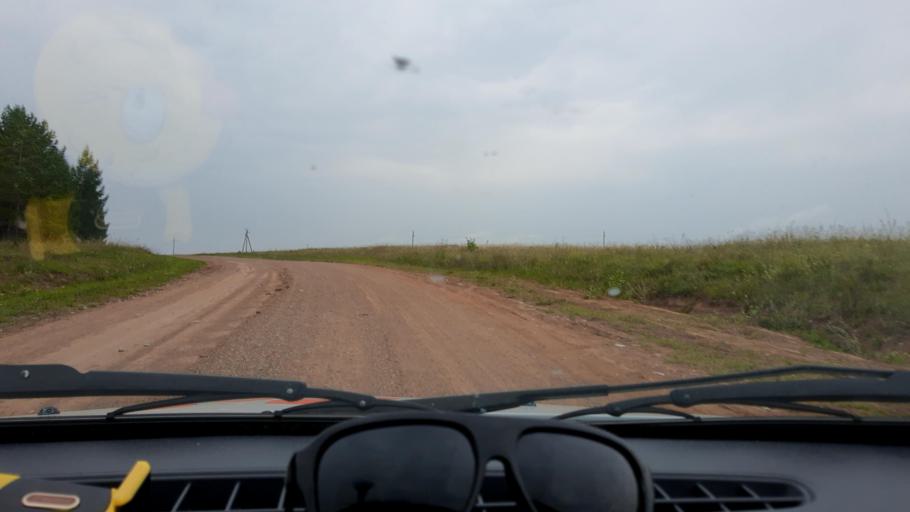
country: RU
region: Bashkortostan
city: Asanovo
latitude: 54.9615
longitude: 55.6719
